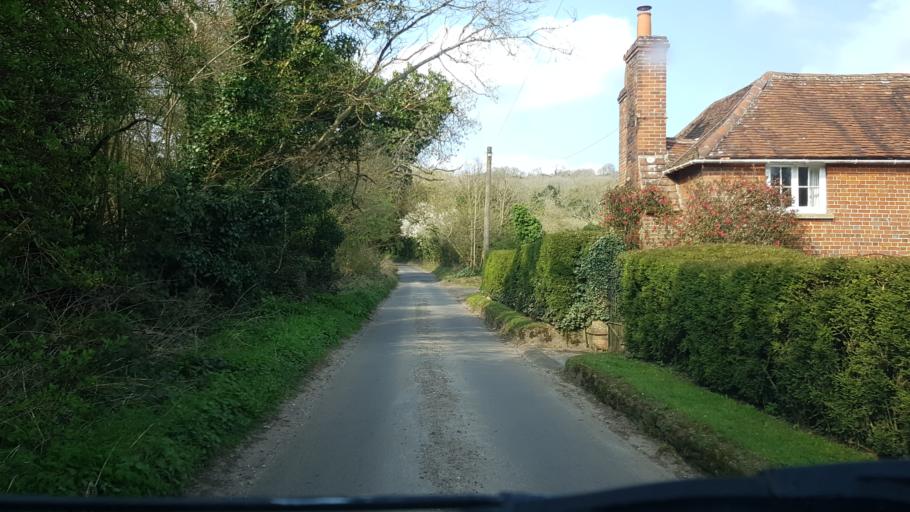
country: GB
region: England
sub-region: Surrey
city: Chilworth
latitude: 51.2281
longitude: -0.5205
